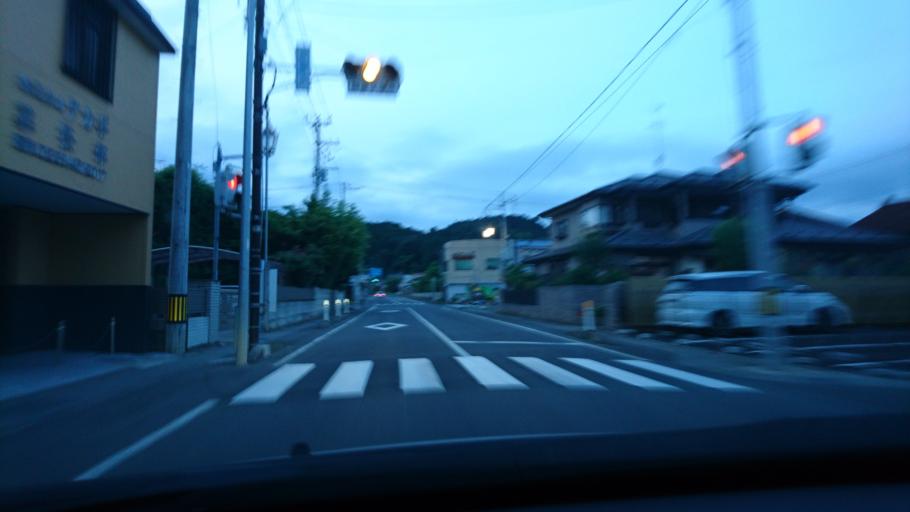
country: JP
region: Iwate
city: Ichinoseki
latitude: 38.8309
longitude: 140.9868
